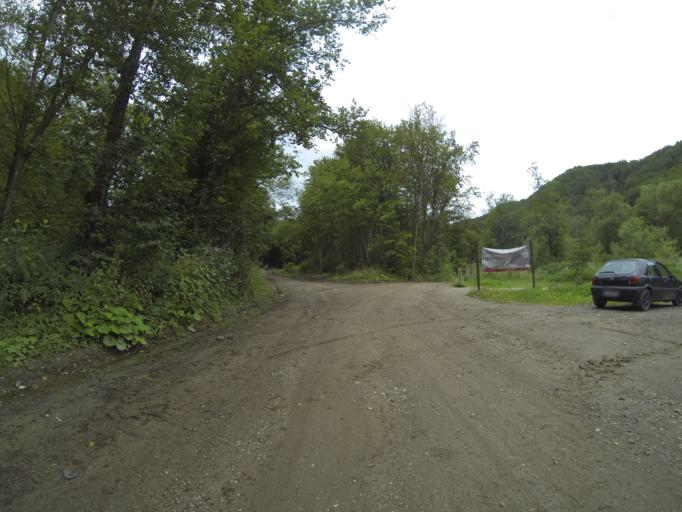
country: RO
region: Brasov
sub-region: Comuna Sinca Veche
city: Sinca Veche
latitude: 45.6961
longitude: 25.1695
